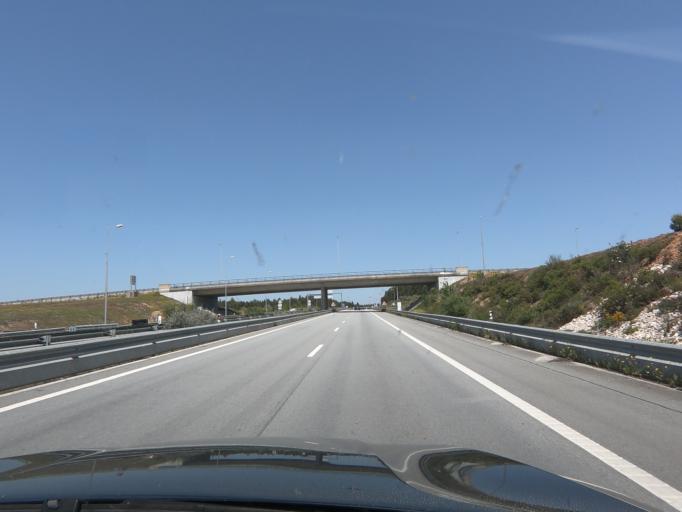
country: PT
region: Santarem
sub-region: Entroncamento
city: Entroncamento
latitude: 39.4941
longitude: -8.4435
